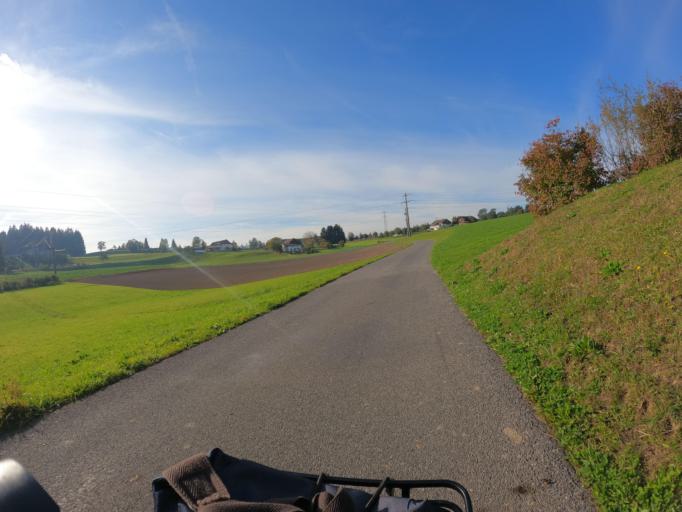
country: CH
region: Aargau
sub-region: Bezirk Muri
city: Aristau
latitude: 47.2754
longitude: 8.3584
